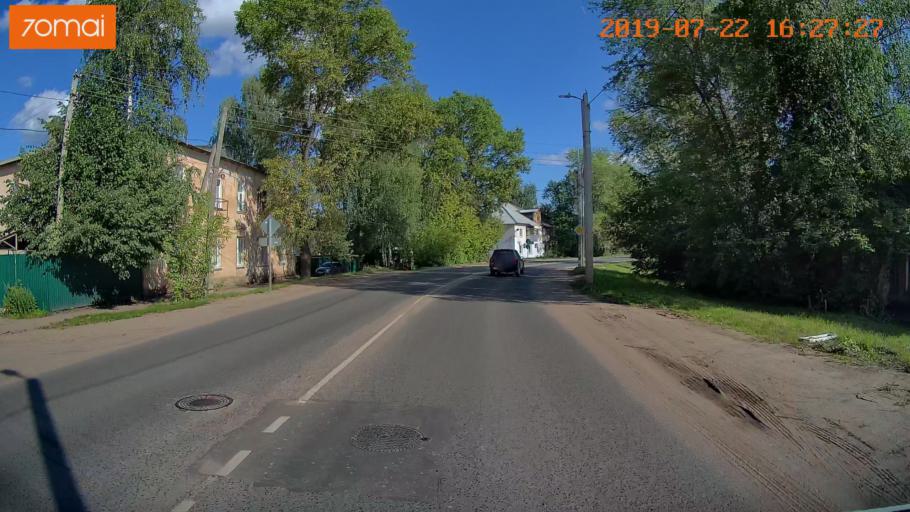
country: RU
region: Ivanovo
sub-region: Gorod Ivanovo
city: Ivanovo
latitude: 57.0440
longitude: 40.9458
